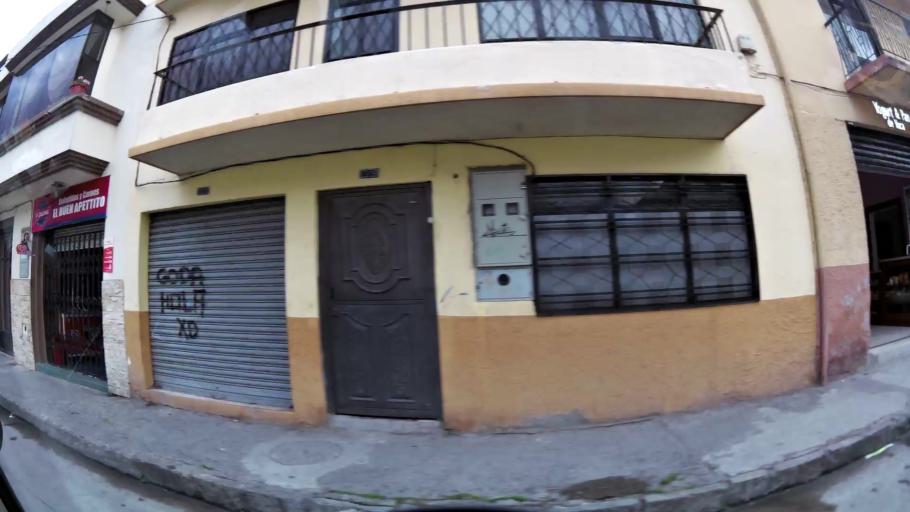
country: EC
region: Azuay
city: Cuenca
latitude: -2.8907
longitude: -79.0082
